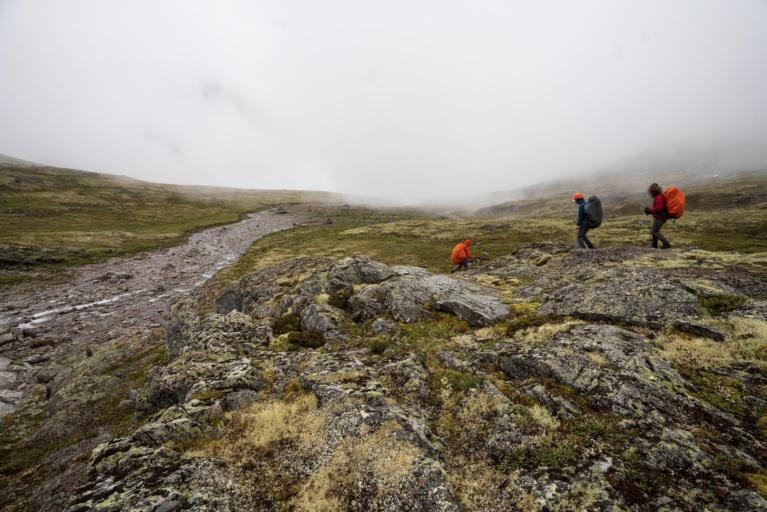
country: RU
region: Transbaikal Territory
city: Chara
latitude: 56.8608
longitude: 117.4666
